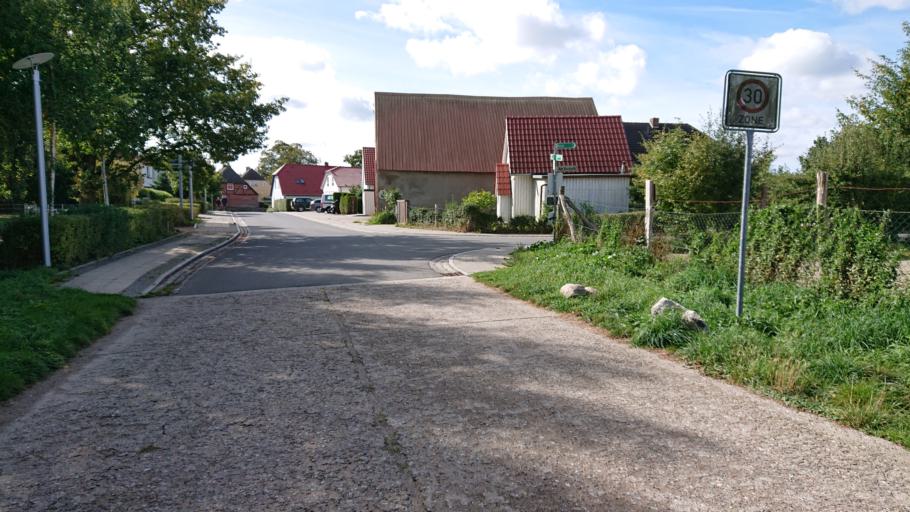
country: DE
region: Mecklenburg-Vorpommern
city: Altefahr
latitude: 54.3318
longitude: 13.1267
